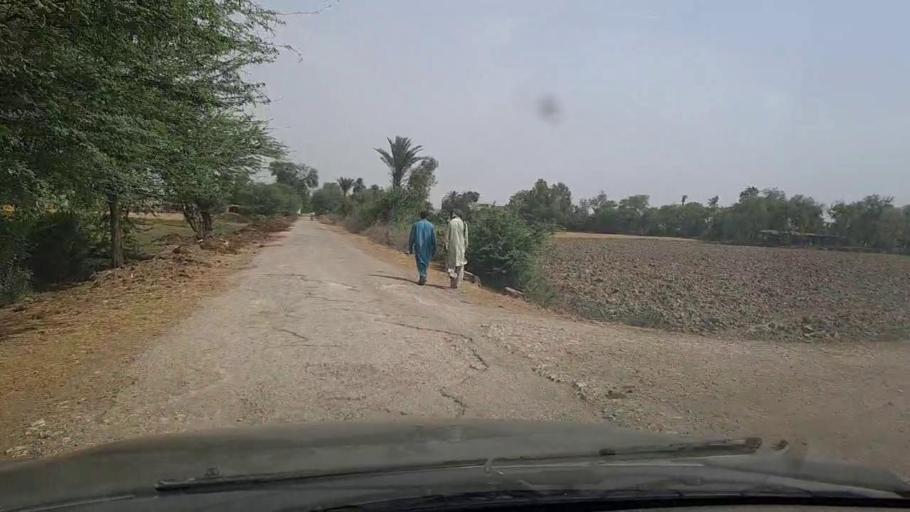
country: PK
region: Sindh
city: Lakhi
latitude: 27.8434
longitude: 68.7597
